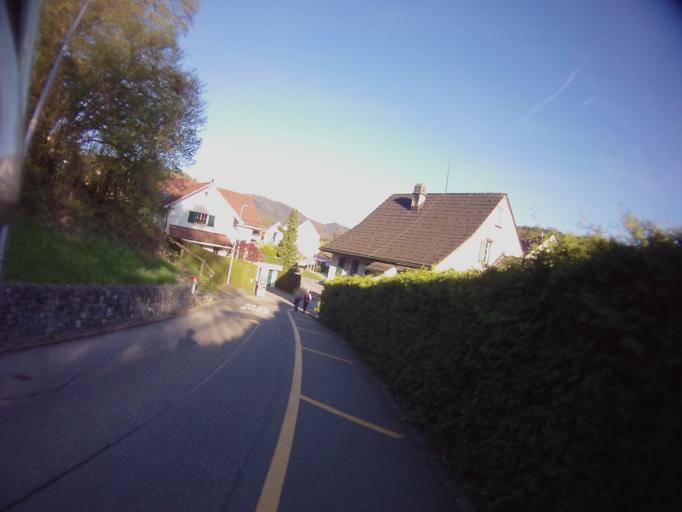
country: CH
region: Zurich
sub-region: Bezirk Dietikon
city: Birmensdorf
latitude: 47.3563
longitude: 8.4408
